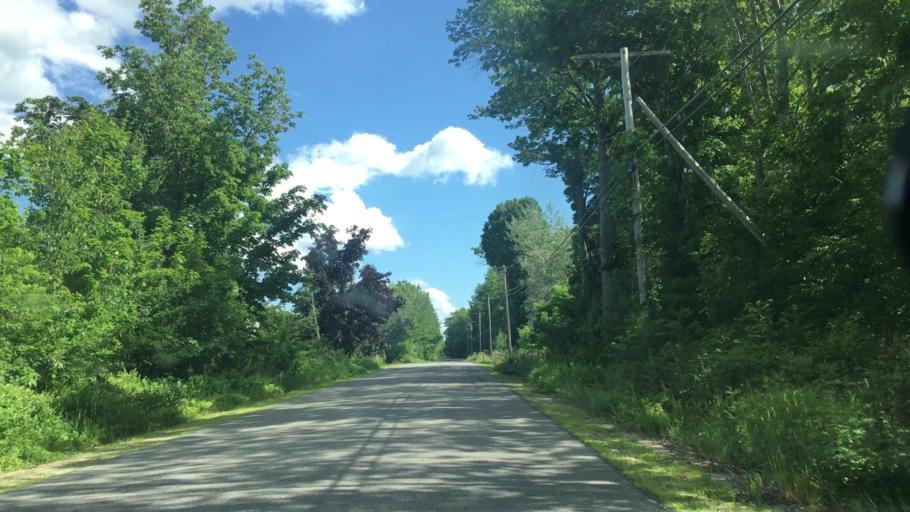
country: US
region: Maine
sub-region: Franklin County
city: Wilton
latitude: 44.6392
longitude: -70.2001
